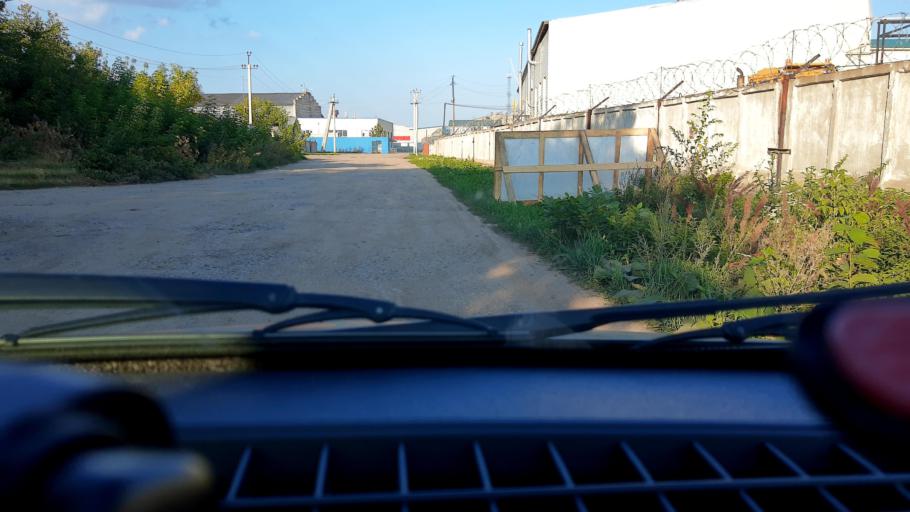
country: RU
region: Bashkortostan
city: Ufa
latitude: 54.5668
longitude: 55.9261
